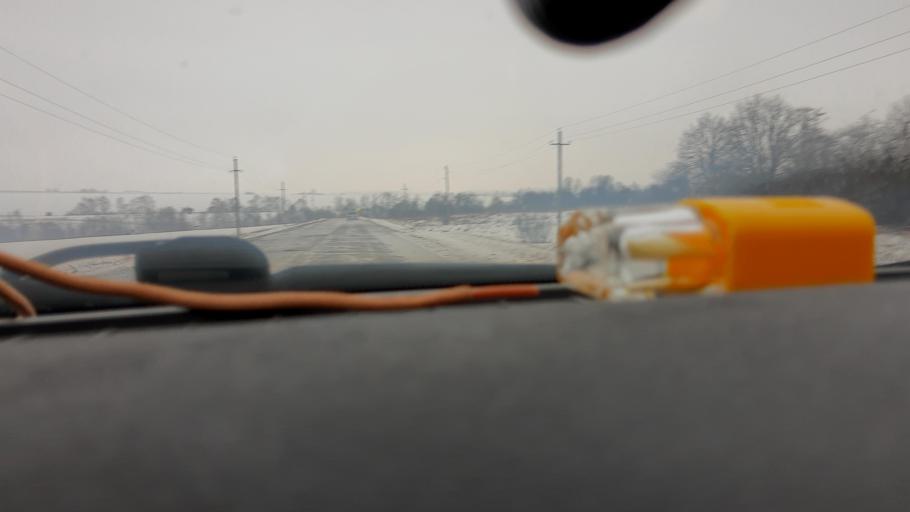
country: RU
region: Bashkortostan
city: Ulukulevo
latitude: 54.5294
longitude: 56.4294
